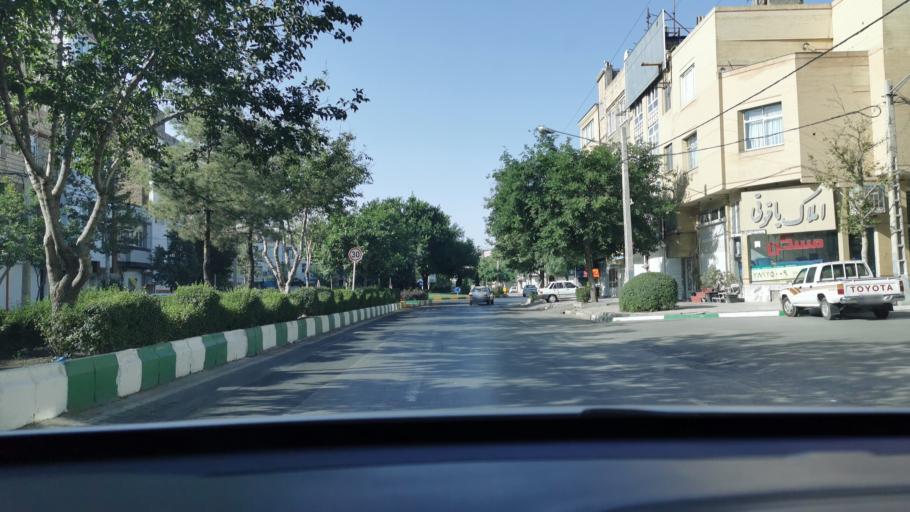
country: IR
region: Razavi Khorasan
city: Mashhad
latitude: 36.3383
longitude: 59.5133
